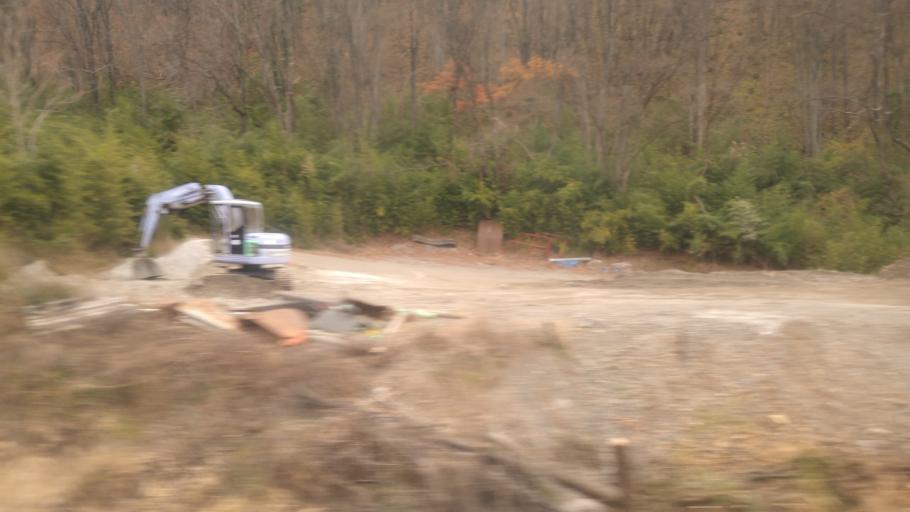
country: JP
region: Nagano
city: Matsumoto
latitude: 36.2530
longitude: 137.9518
